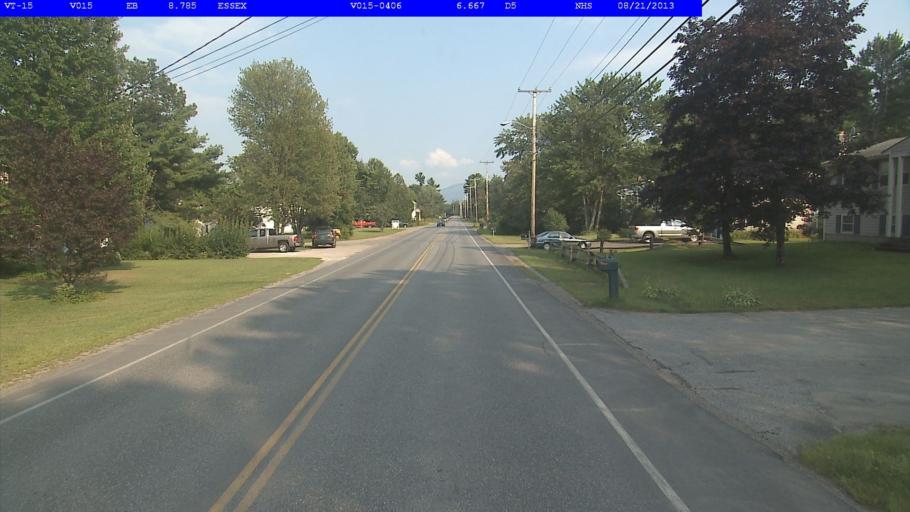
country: US
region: Vermont
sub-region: Chittenden County
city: Jericho
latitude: 44.5039
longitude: -73.0360
